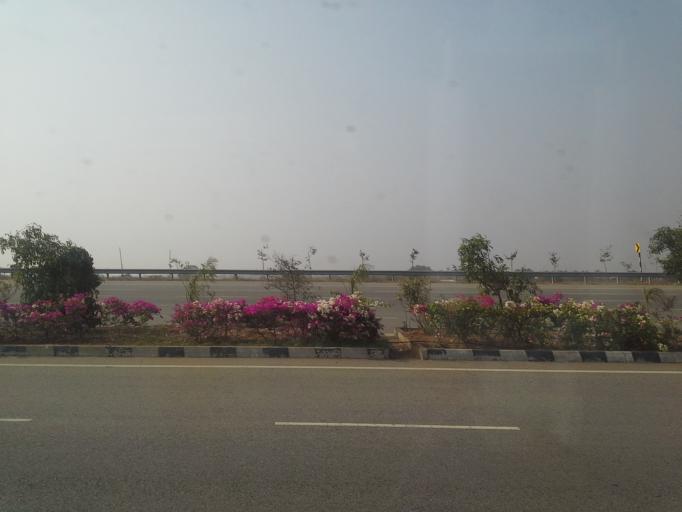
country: IN
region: Telangana
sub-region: Rangareddi
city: Sriramnagar
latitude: 17.2050
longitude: 78.3911
